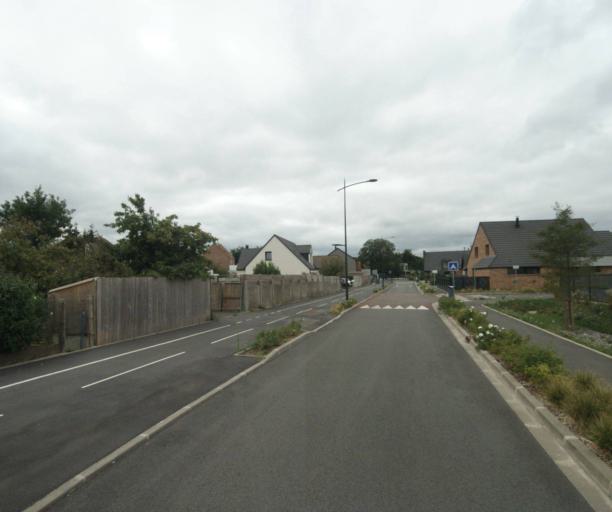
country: FR
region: Nord-Pas-de-Calais
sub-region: Departement du Nord
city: Lesquin
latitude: 50.5928
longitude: 3.1193
